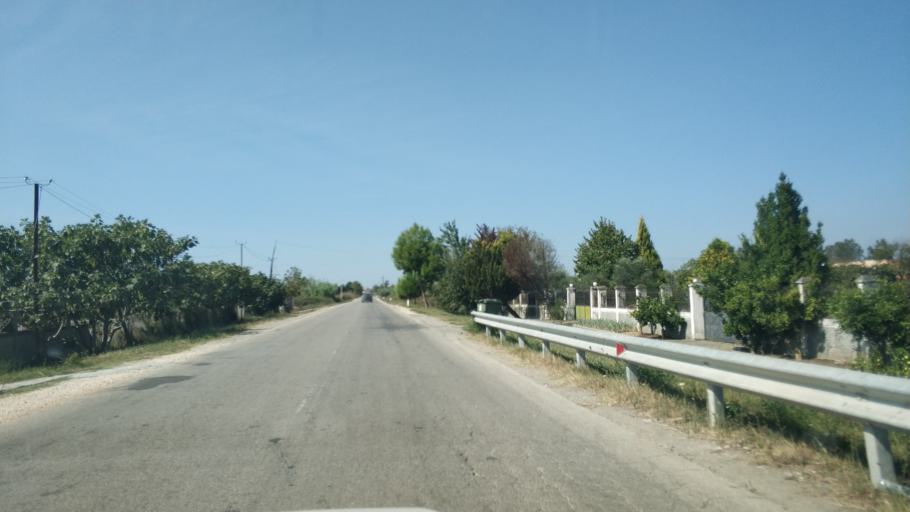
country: AL
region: Fier
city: Terbuf
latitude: 41.0520
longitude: 19.5911
